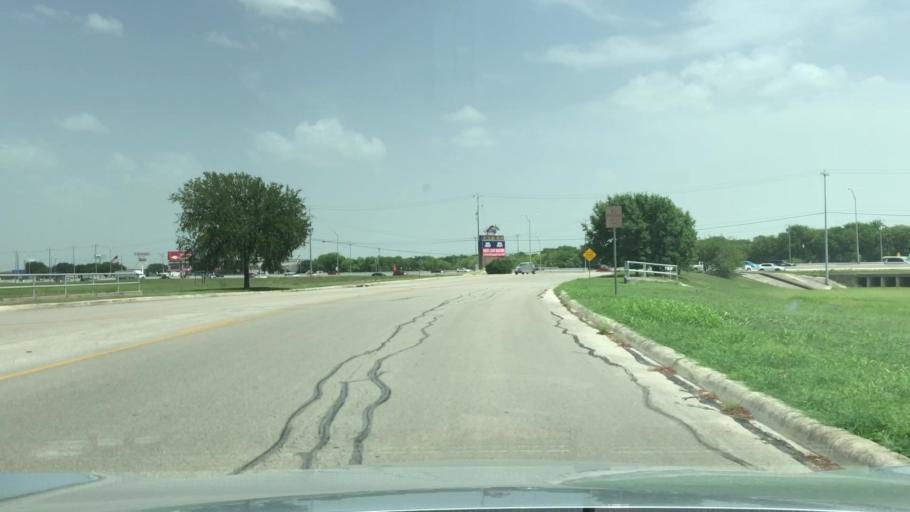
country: US
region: Texas
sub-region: Bexar County
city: Selma
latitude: 29.5816
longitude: -98.3149
